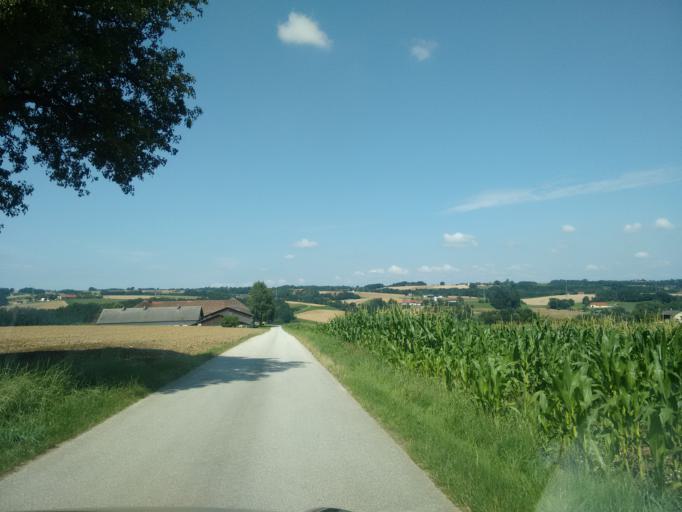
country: AT
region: Upper Austria
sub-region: Politischer Bezirk Kirchdorf an der Krems
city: Kremsmunster
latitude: 48.0122
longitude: 14.1267
